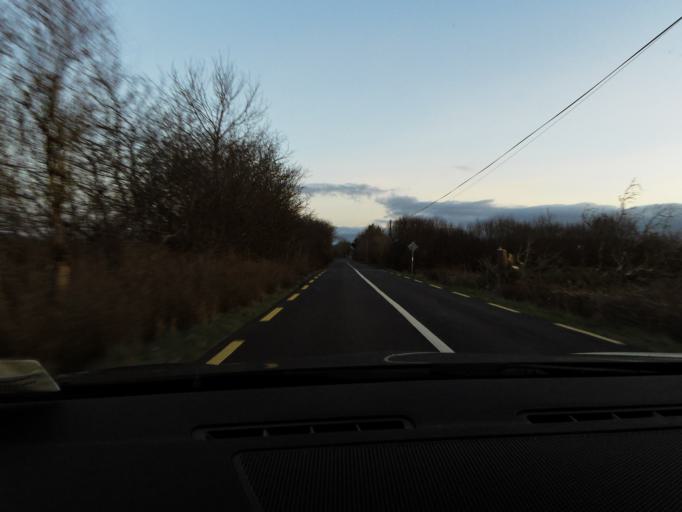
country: IE
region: Connaught
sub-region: Roscommon
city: Boyle
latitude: 53.8938
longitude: -8.2508
